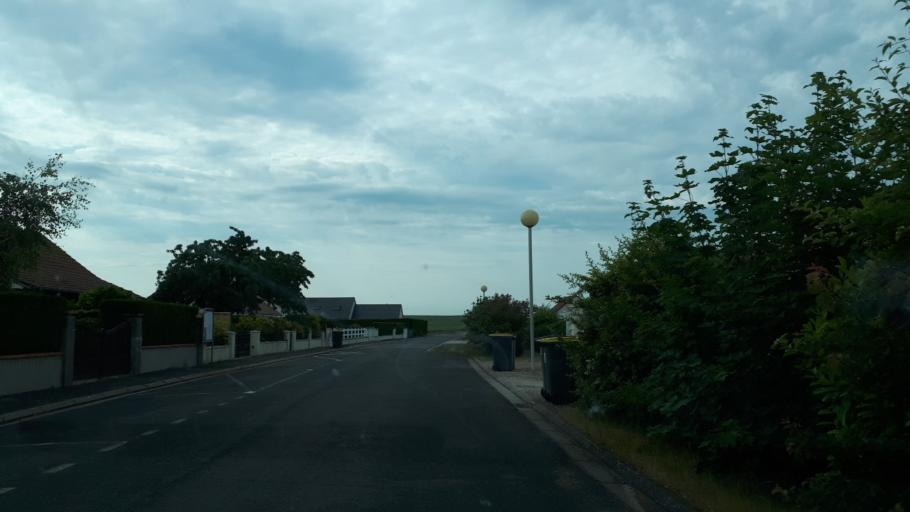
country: FR
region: Centre
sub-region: Departement du Loir-et-Cher
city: Naveil
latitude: 47.7698
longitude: 1.0113
